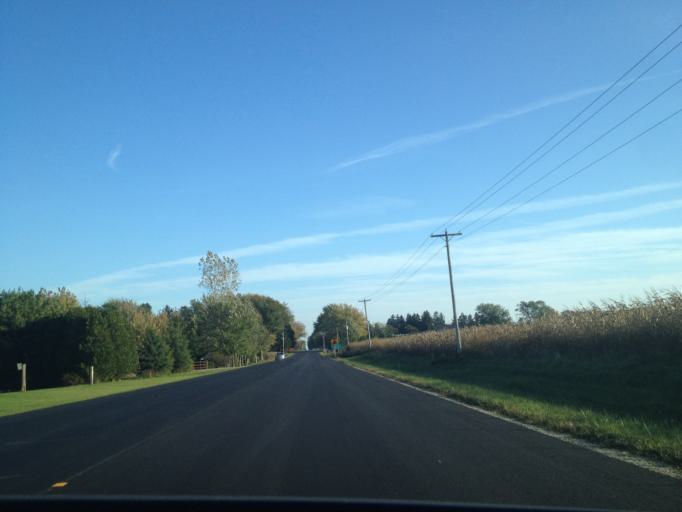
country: CA
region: Ontario
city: Delaware
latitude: 42.5708
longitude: -81.5662
